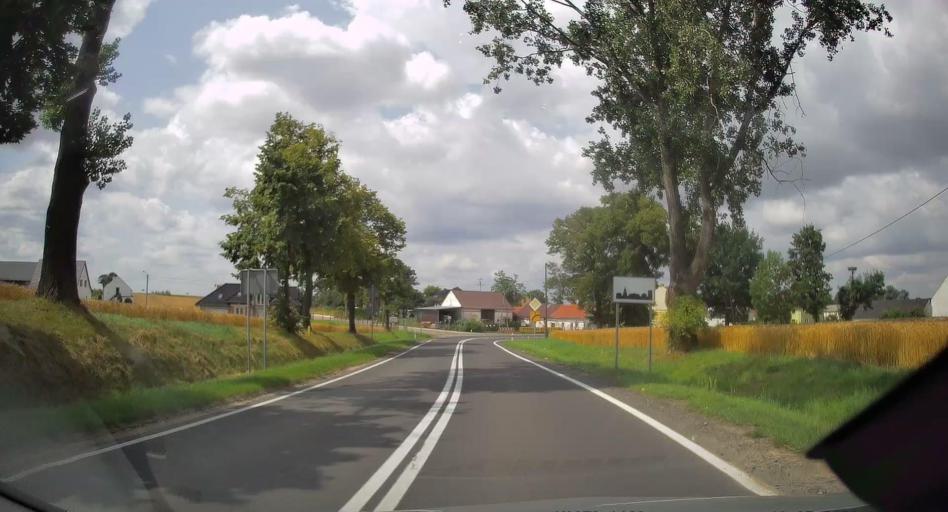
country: PL
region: Opole Voivodeship
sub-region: Powiat prudnicki
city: Twardawa
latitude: 50.3353
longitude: 17.9708
